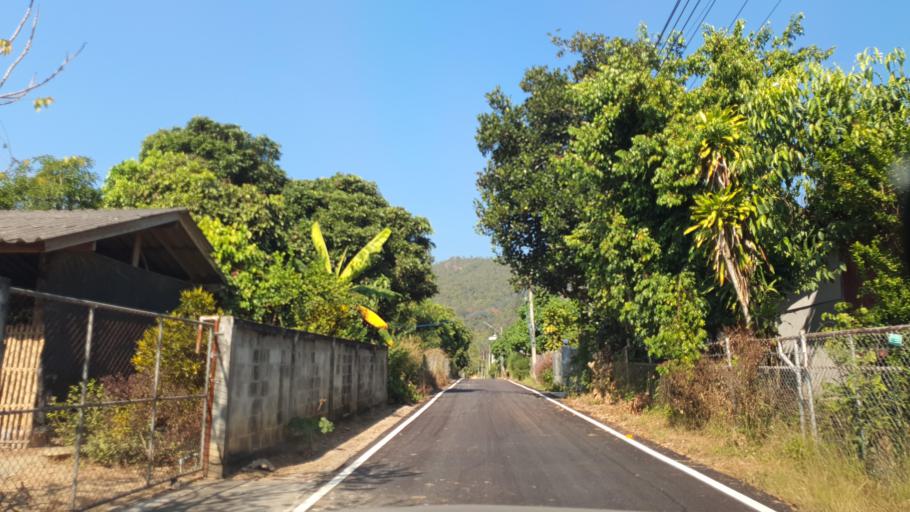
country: TH
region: Lamphun
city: Mae Tha
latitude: 18.5553
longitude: 99.2500
